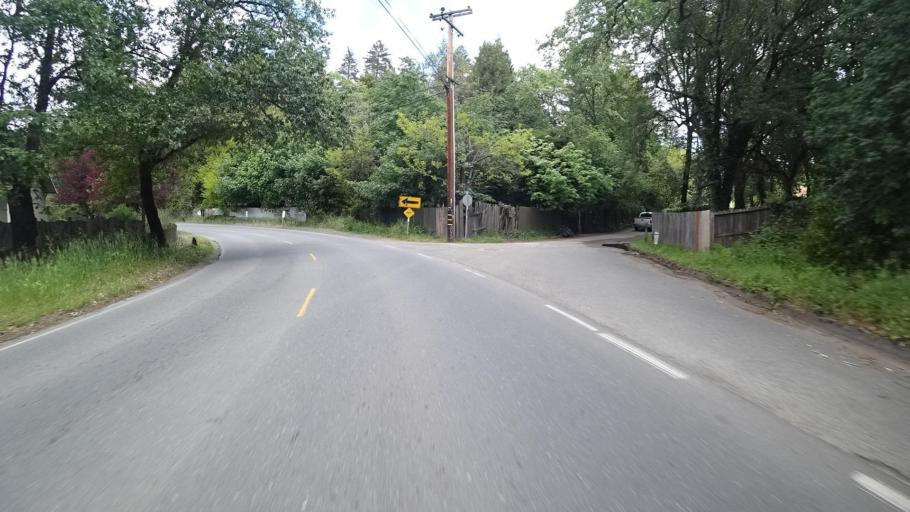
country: US
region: California
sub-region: Humboldt County
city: Redway
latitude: 40.1234
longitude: -123.8303
